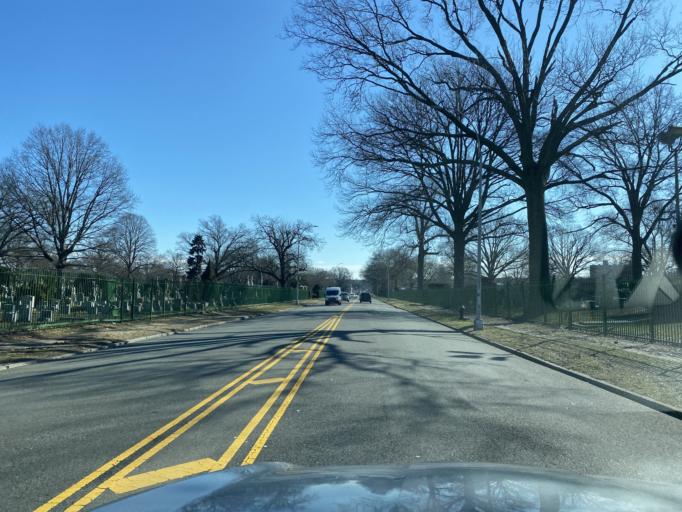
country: US
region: New York
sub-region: Queens County
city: Borough of Queens
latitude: 40.7129
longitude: -73.8674
